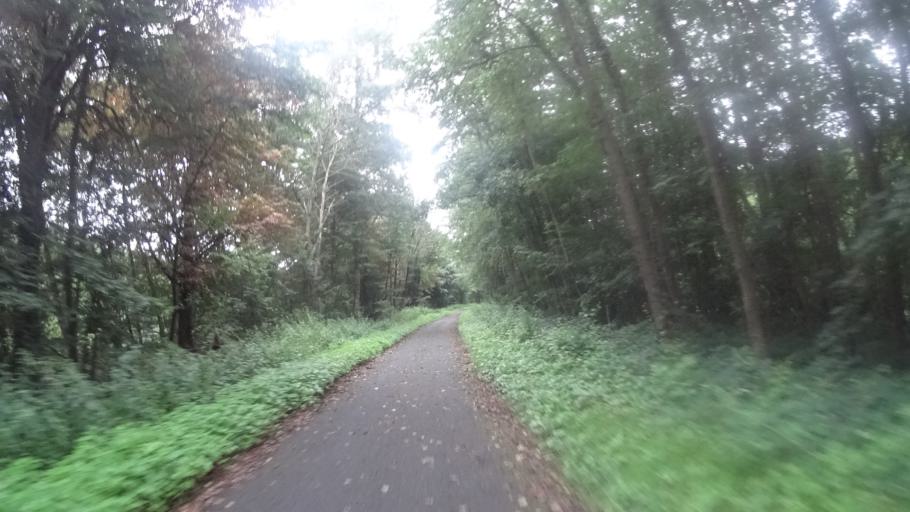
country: FR
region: Lorraine
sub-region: Departement de Meurthe-et-Moselle
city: Velaine-en-Haye
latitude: 48.6611
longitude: 6.0184
